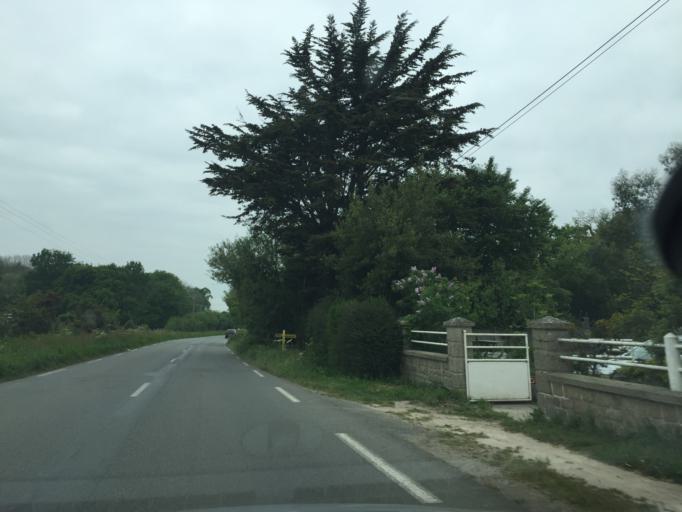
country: FR
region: Brittany
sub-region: Departement des Cotes-d'Armor
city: Matignon
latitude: 48.5947
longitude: -2.2675
